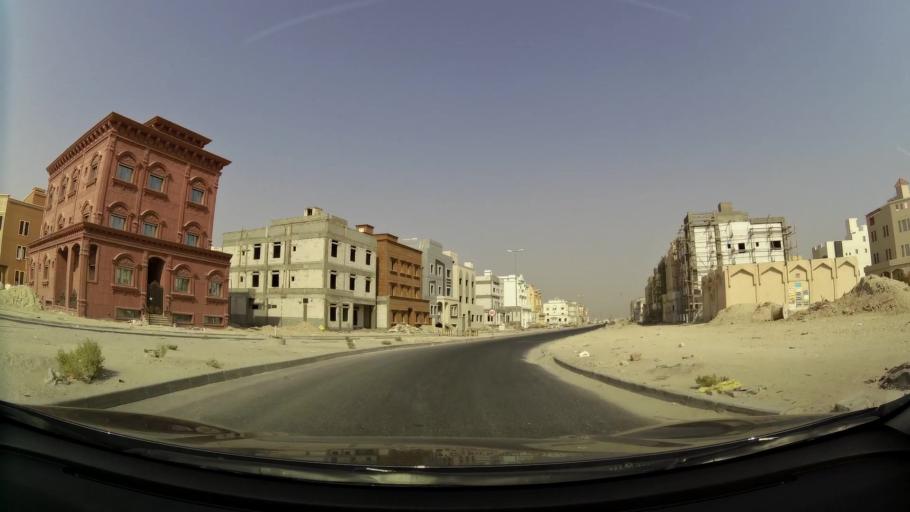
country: KW
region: Muhafazat al Jahra'
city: Al Jahra'
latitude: 29.3544
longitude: 47.7702
